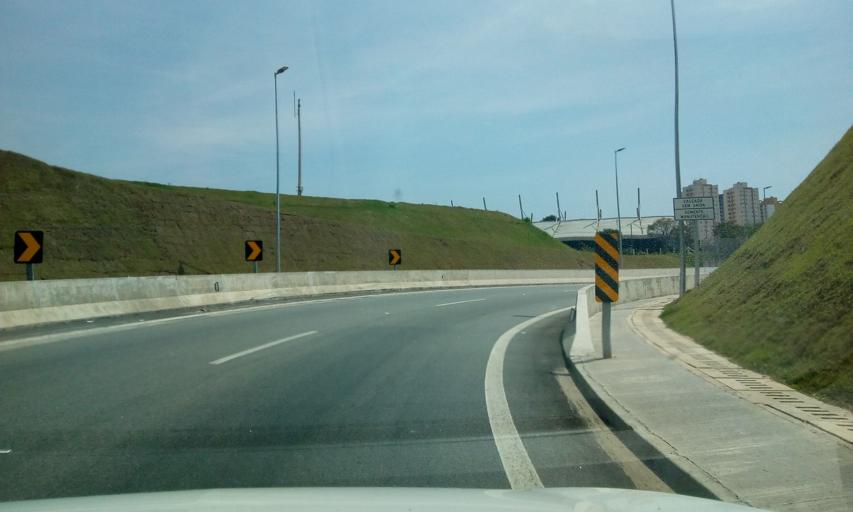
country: BR
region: Sao Paulo
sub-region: Jundiai
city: Jundiai
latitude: -23.2100
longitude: -46.8956
